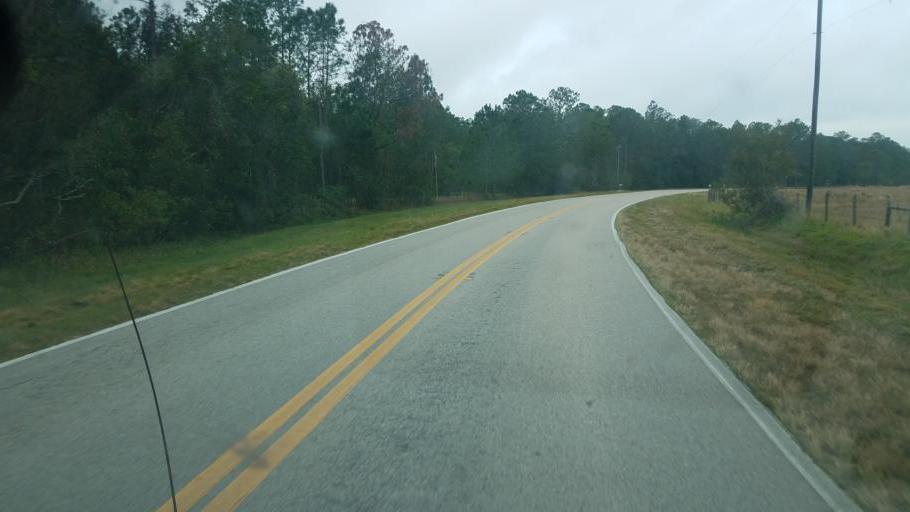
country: US
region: Florida
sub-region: Polk County
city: Polk City
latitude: 28.2570
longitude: -81.7356
